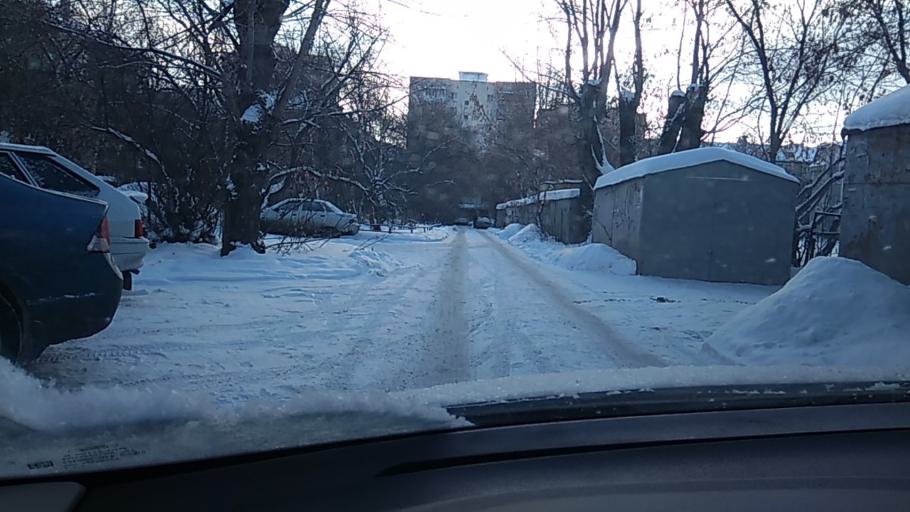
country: RU
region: Sverdlovsk
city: Yekaterinburg
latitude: 56.8108
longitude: 60.6159
